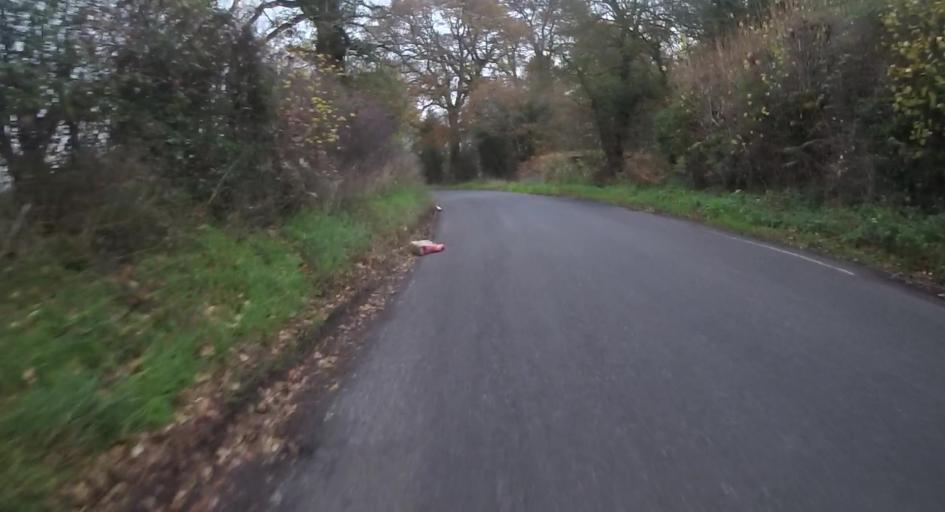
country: GB
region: England
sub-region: Wokingham
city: Swallowfield
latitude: 51.3819
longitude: -0.9352
